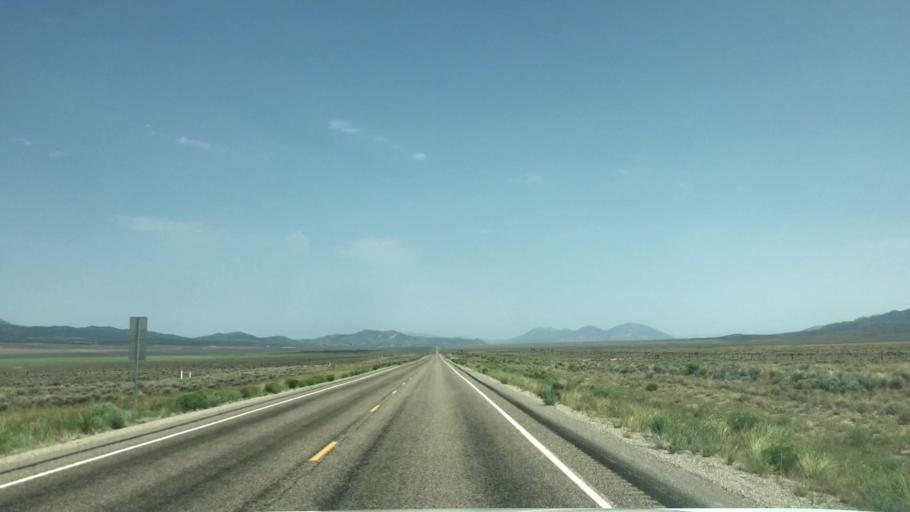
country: US
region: Nevada
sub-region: White Pine County
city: Ely
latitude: 39.0934
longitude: -114.7553
